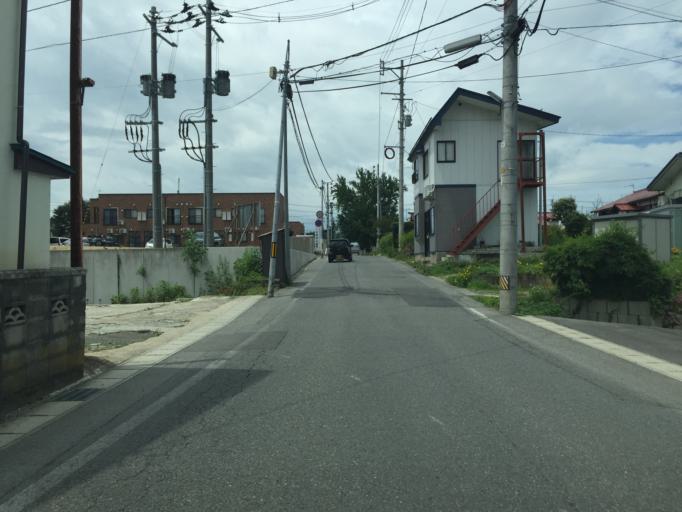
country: JP
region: Yamagata
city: Yonezawa
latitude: 37.9133
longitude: 140.1243
